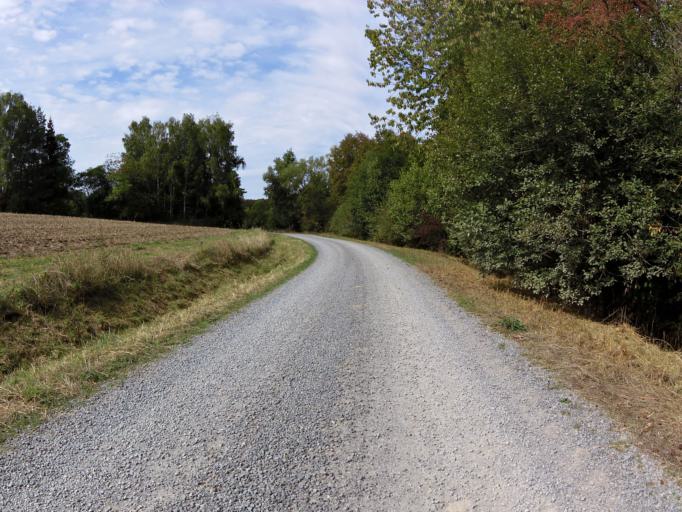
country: DE
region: Bavaria
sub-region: Regierungsbezirk Unterfranken
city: Hettstadt
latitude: 49.7799
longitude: 9.8168
